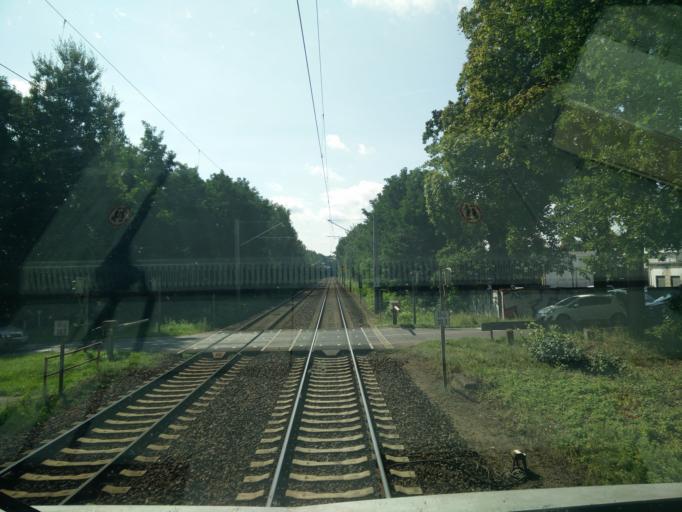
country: DE
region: Brandenburg
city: Bestensee
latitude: 52.2727
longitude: 13.6341
